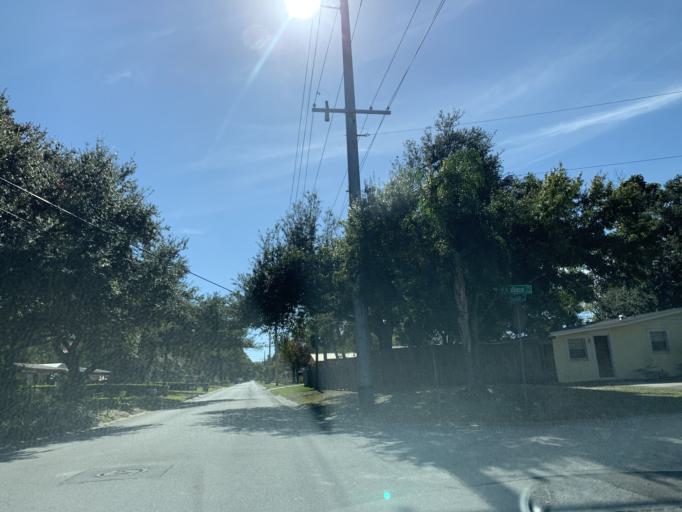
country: US
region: Florida
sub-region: Hillsborough County
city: Tampa
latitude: 27.8854
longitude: -82.4981
